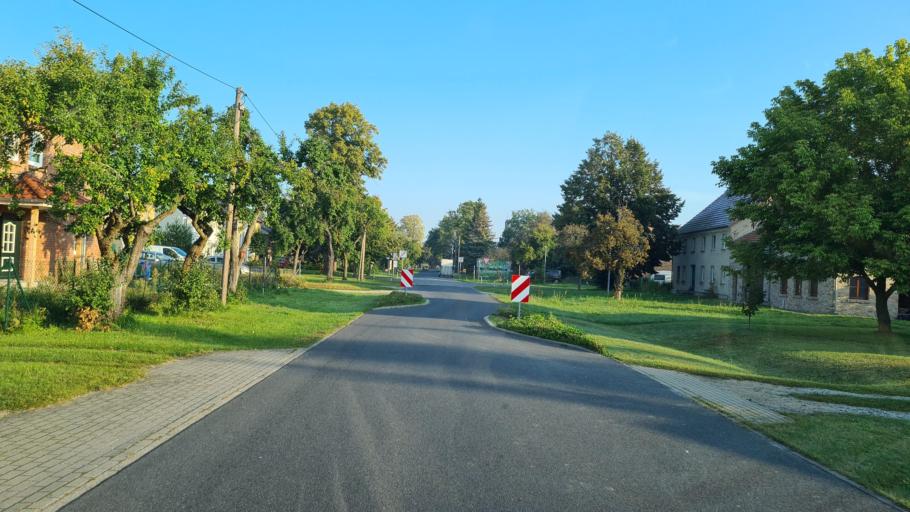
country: DE
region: Brandenburg
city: Luckenwalde
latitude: 52.0981
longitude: 13.0734
